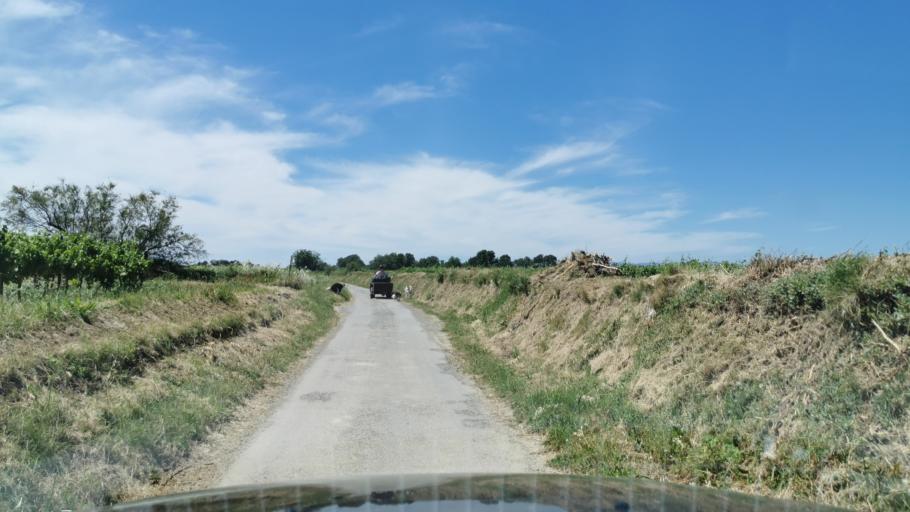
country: FR
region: Languedoc-Roussillon
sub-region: Departement de l'Aude
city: Nevian
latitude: 43.2171
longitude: 2.8921
